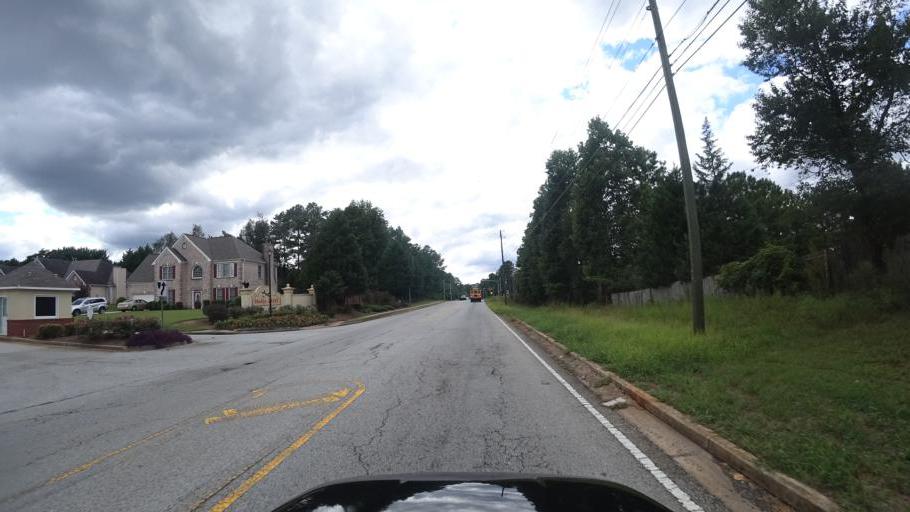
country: US
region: Georgia
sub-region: DeKalb County
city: Panthersville
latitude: 33.6553
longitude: -84.2290
